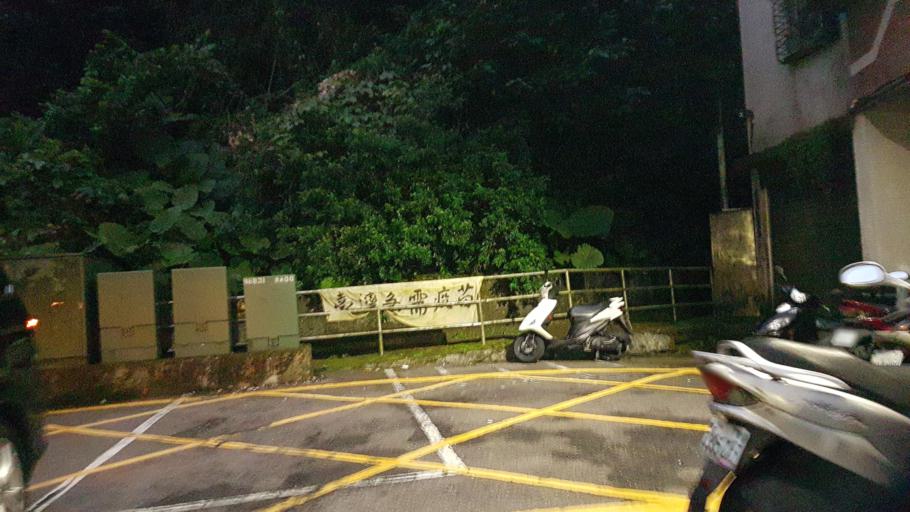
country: TW
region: Taipei
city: Taipei
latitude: 24.9948
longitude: 121.5480
